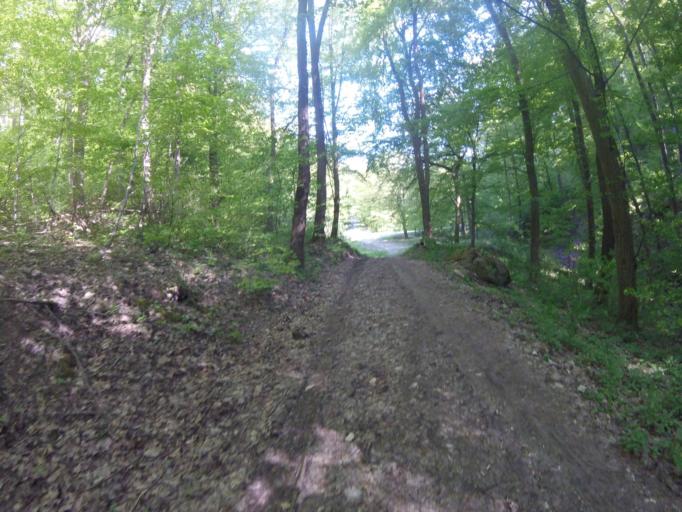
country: HU
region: Pest
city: Pilisszentkereszt
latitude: 47.7087
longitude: 18.8961
